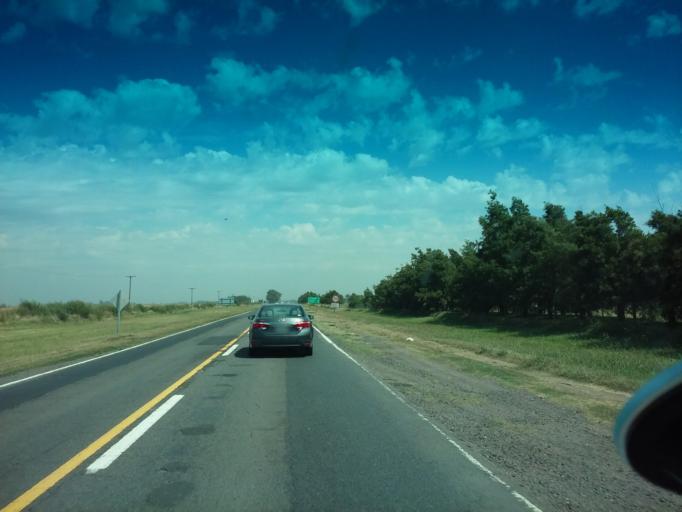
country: AR
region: Buenos Aires
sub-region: Partido de Carlos Casares
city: Carlos Casares
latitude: -35.6145
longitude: -61.2656
